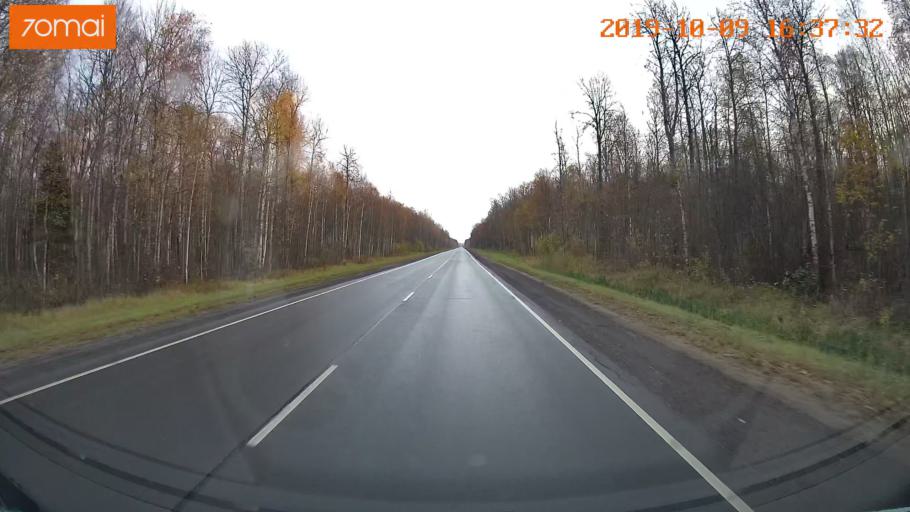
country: RU
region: Kostroma
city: Volgorechensk
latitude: 57.5254
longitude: 41.0259
